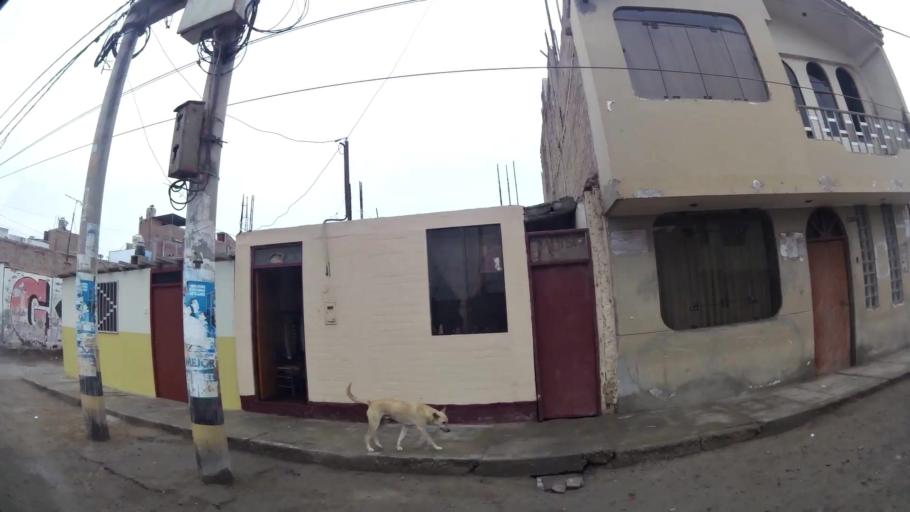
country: PE
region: Ica
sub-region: Provincia de Pisco
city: Pisco
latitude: -13.7330
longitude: -76.2237
